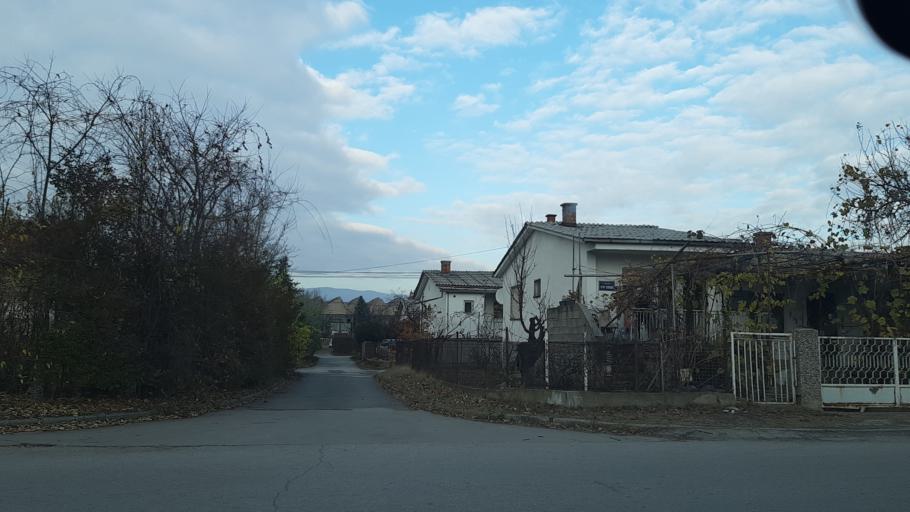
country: MK
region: Kisela Voda
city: Usje
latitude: 41.9756
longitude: 21.4552
